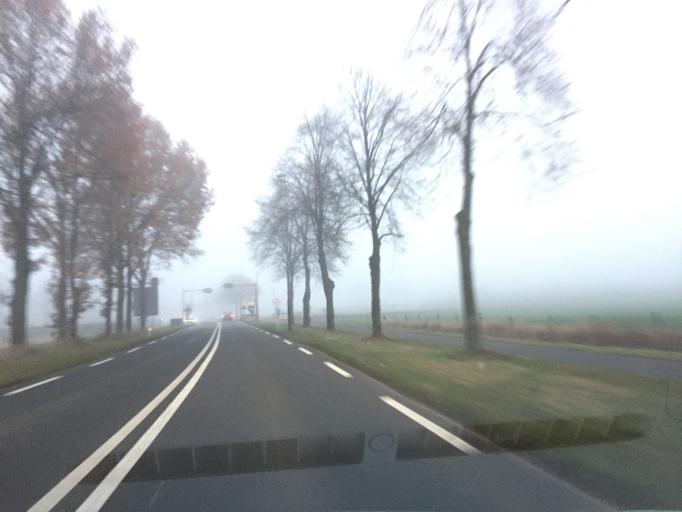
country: NL
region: Gelderland
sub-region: Gemeente Doetinchem
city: Doetinchem
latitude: 51.9571
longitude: 6.2201
